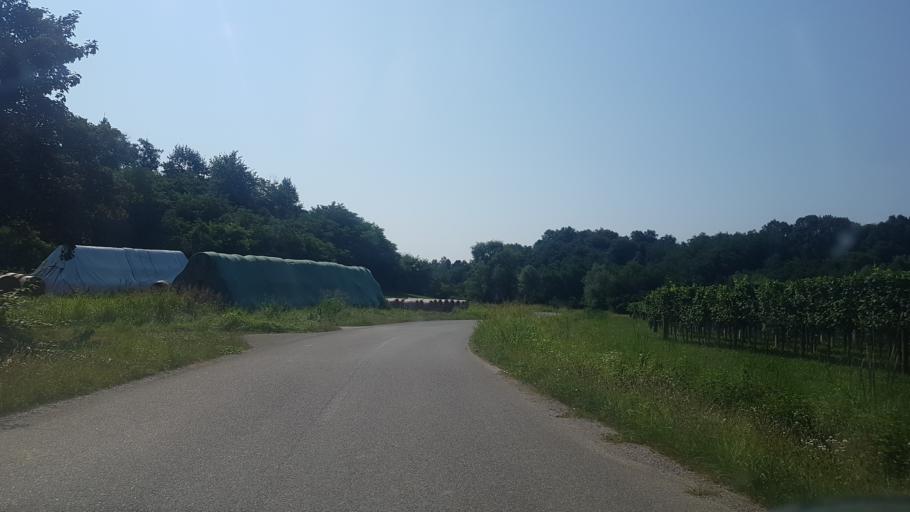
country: IT
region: Friuli Venezia Giulia
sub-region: Provincia di Gorizia
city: Mossa
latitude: 45.9554
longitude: 13.5661
